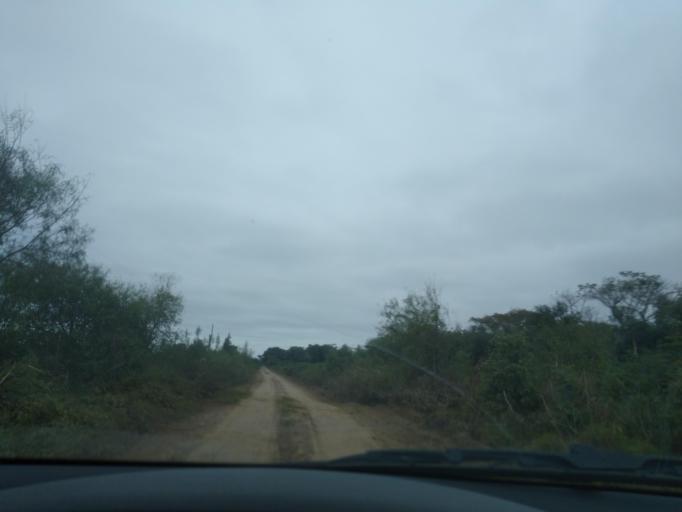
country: AR
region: Chaco
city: Colonia Benitez
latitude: -27.3721
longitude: -58.9464
